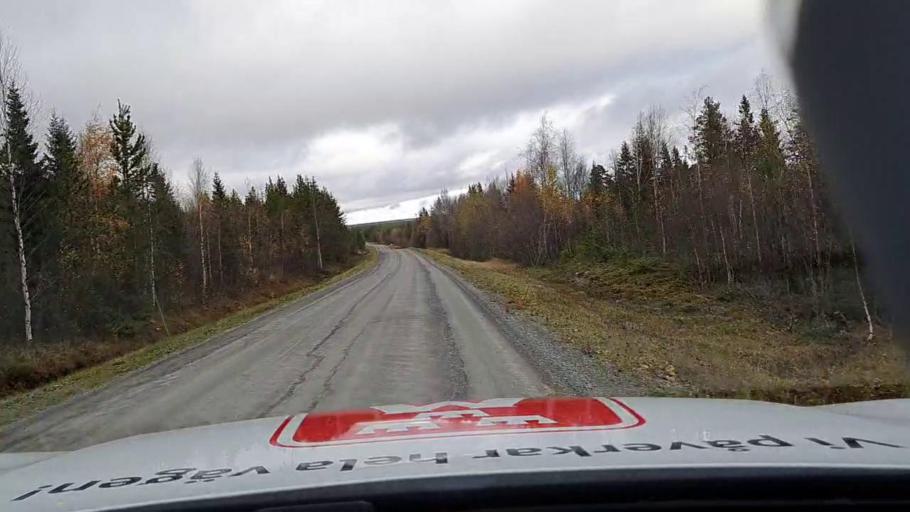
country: SE
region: Jaemtland
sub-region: Krokoms Kommun
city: Valla
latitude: 63.0563
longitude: 13.9632
